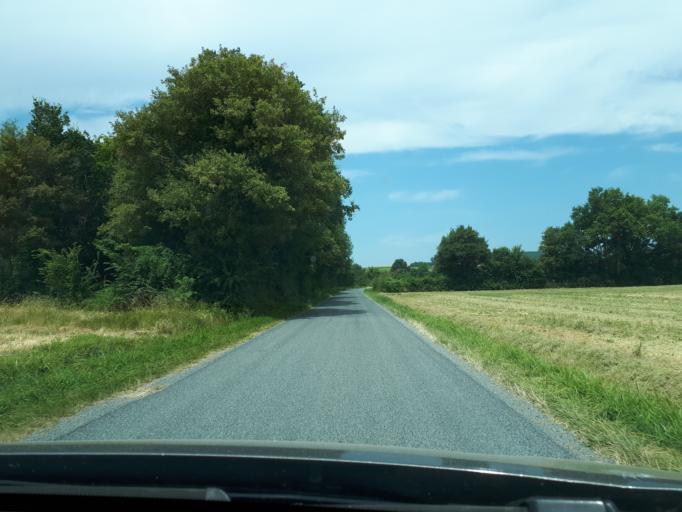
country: FR
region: Centre
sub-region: Departement du Cher
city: Sancerre
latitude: 47.2968
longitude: 2.7494
